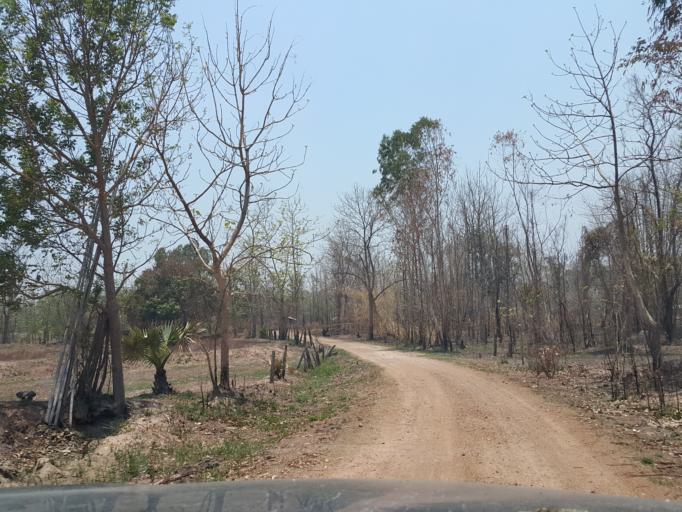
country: TH
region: Lampang
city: Thoen
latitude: 17.6421
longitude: 99.2782
